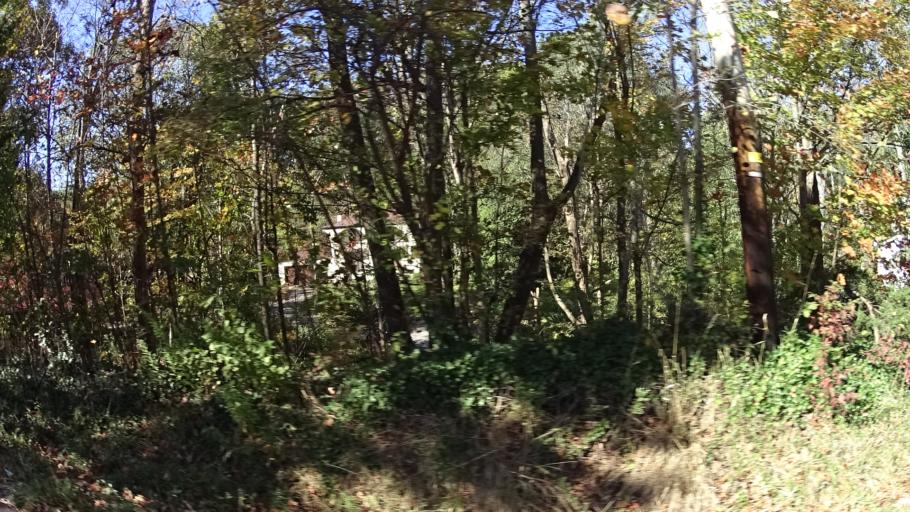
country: US
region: Ohio
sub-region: Lorain County
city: Amherst
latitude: 41.3899
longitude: -82.2398
